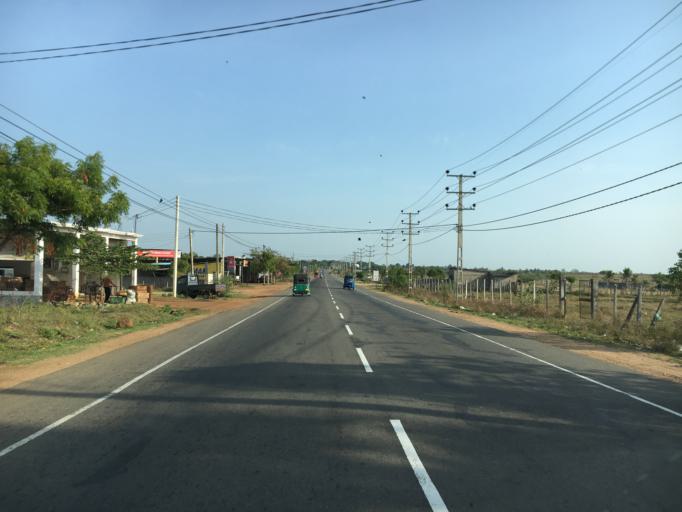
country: LK
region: Eastern Province
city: Eravur Town
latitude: 7.9333
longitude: 81.5110
